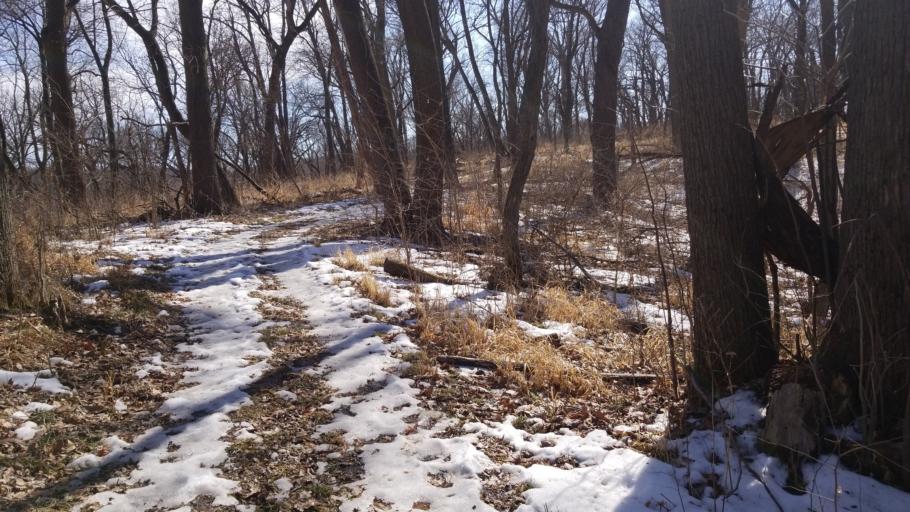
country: US
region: Nebraska
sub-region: Sarpy County
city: Bellevue
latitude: 41.1725
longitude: -95.9009
